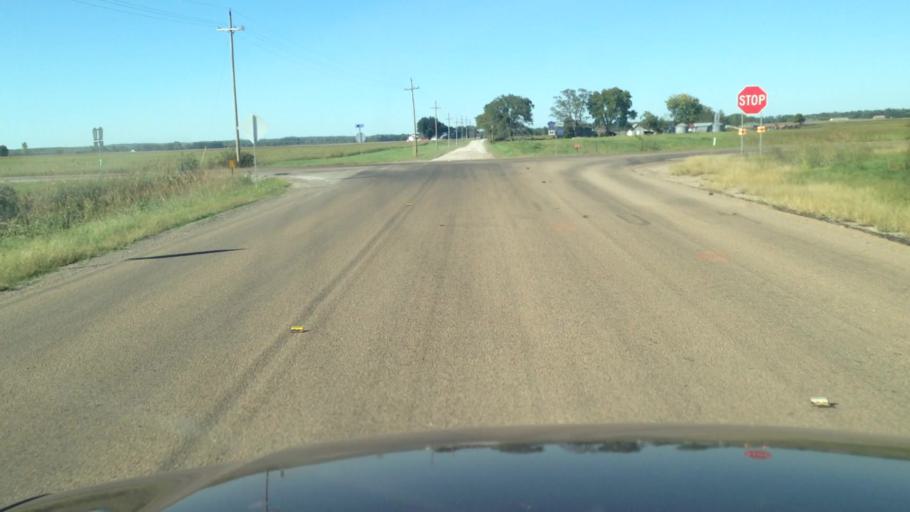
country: US
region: Kansas
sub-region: Douglas County
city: Eudora
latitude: 38.9419
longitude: -95.1489
